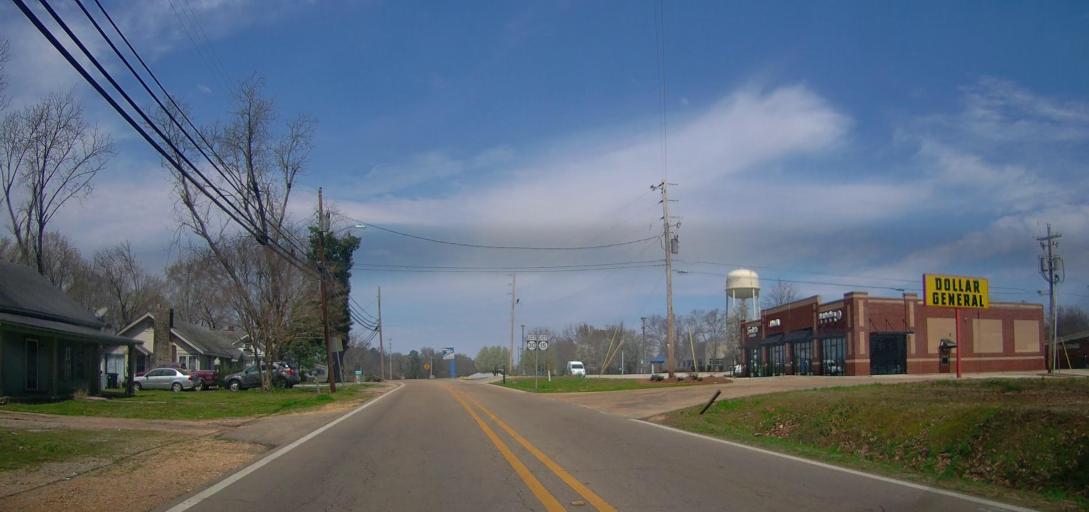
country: US
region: Mississippi
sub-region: Union County
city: New Albany
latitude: 34.4802
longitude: -88.9989
